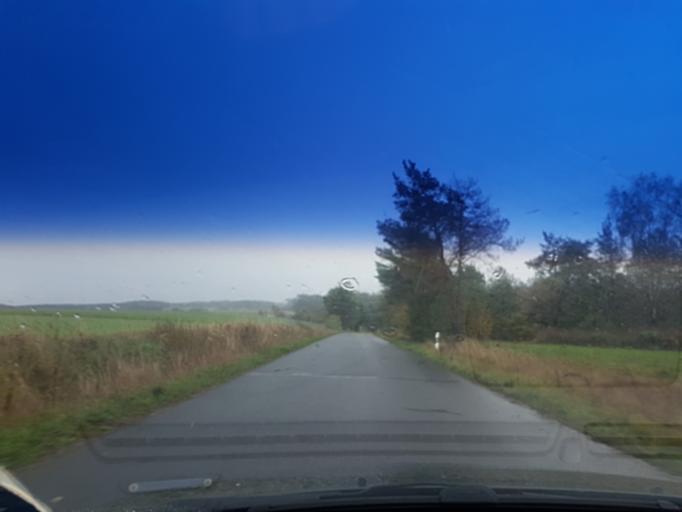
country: DE
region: Bavaria
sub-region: Regierungsbezirk Mittelfranken
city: Markt Taschendorf
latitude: 49.7576
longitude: 10.5451
